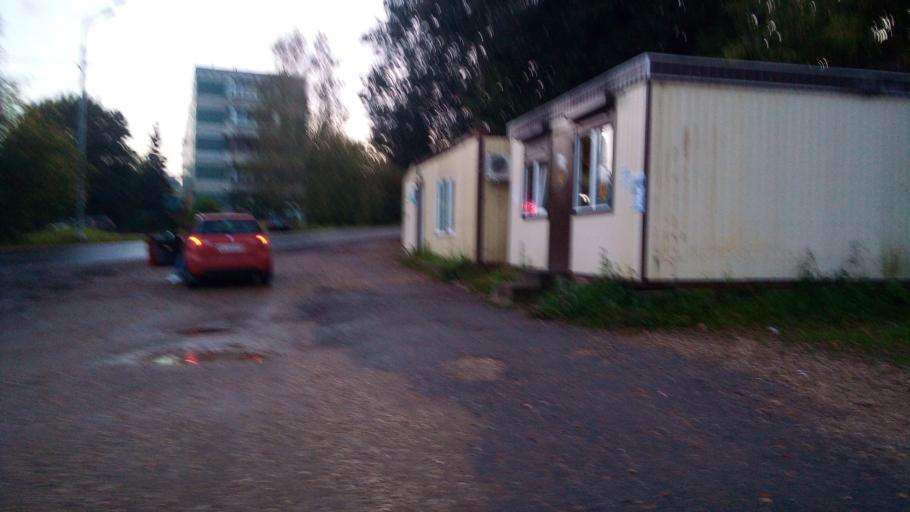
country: RU
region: Moskovskaya
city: Khot'kovo
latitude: 56.2480
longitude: 37.9423
